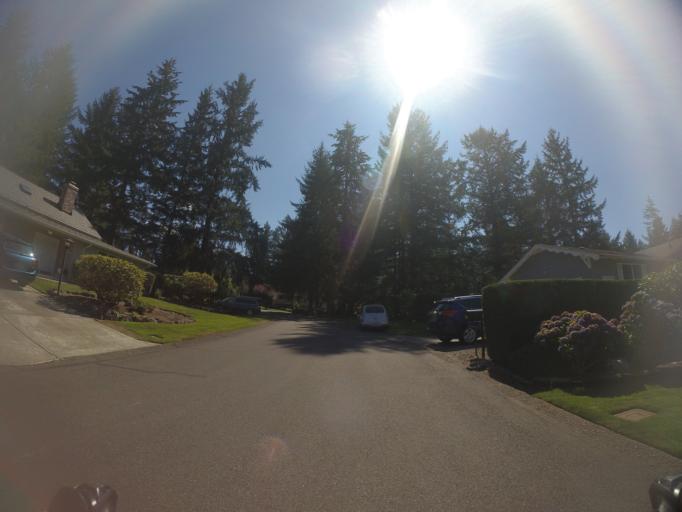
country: US
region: Washington
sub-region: Pierce County
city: University Place
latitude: 47.2148
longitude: -122.5605
